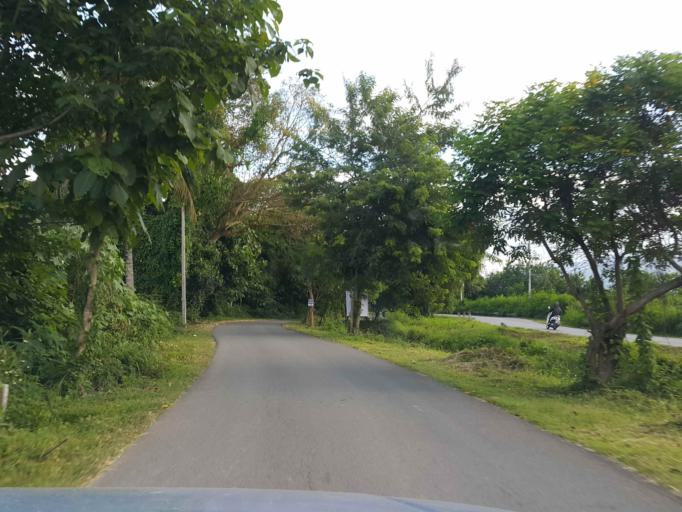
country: TH
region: Chiang Mai
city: San Sai
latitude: 18.9027
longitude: 98.9770
